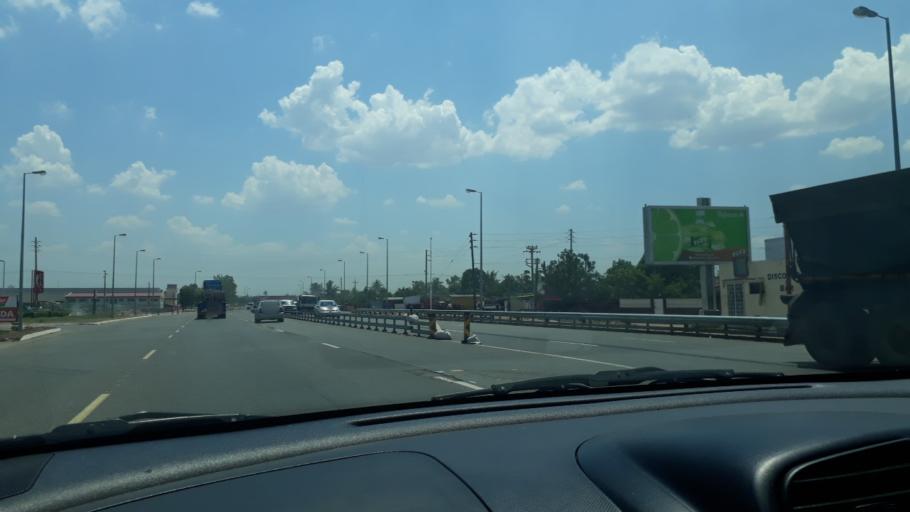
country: MZ
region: Maputo
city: Matola
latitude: -25.9470
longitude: 32.4760
